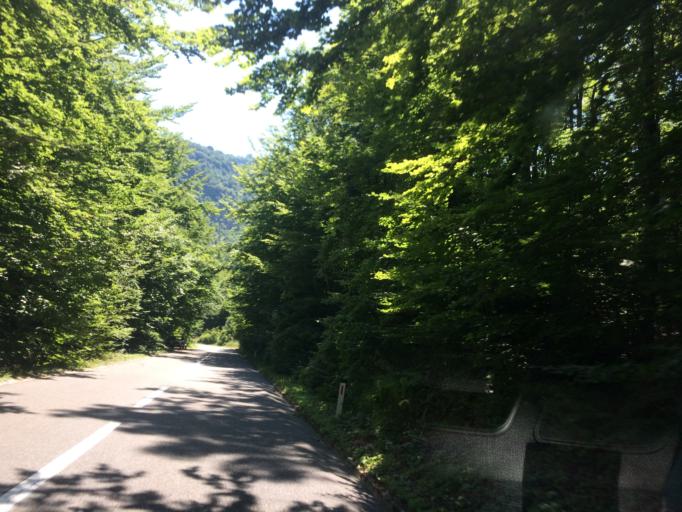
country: ME
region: Opstina Savnik
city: Savnik
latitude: 42.9480
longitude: 19.0963
